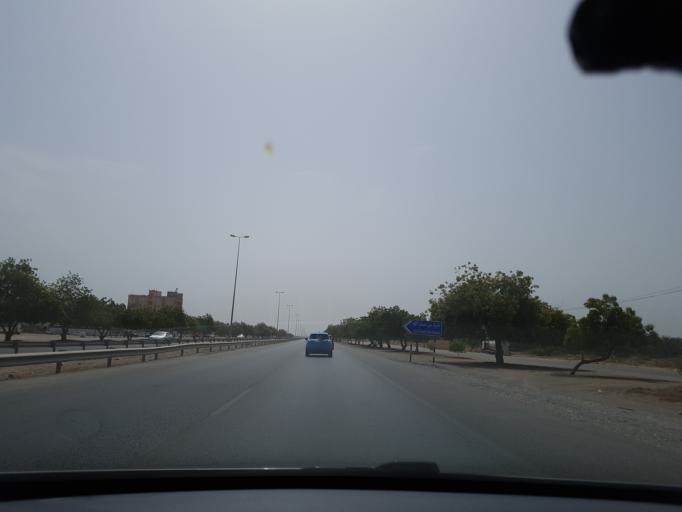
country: OM
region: Al Batinah
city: As Suwayq
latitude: 23.8049
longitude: 57.4736
